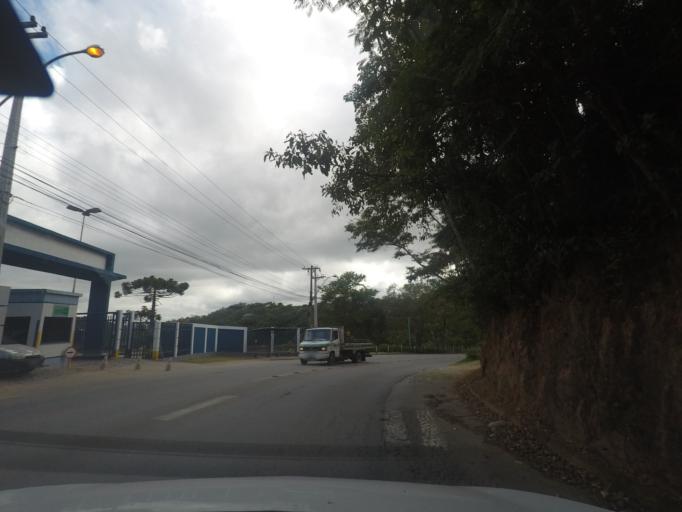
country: BR
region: Rio de Janeiro
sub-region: Teresopolis
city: Teresopolis
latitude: -22.3951
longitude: -42.9595
